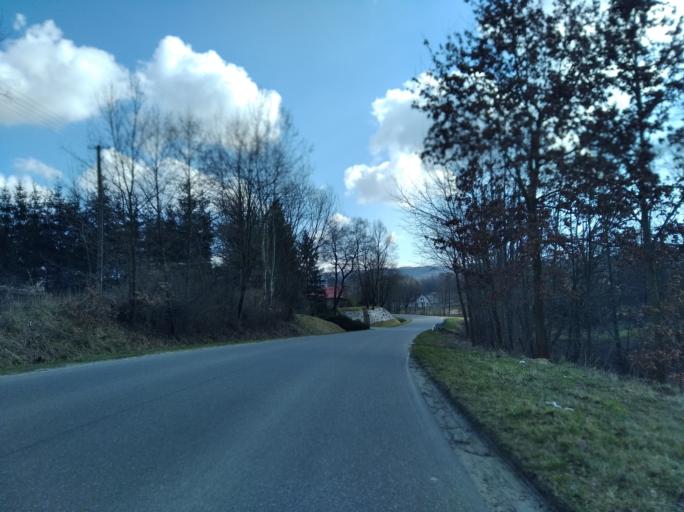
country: PL
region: Subcarpathian Voivodeship
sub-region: Powiat jasielski
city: Kolaczyce
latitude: 49.8582
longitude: 21.4863
